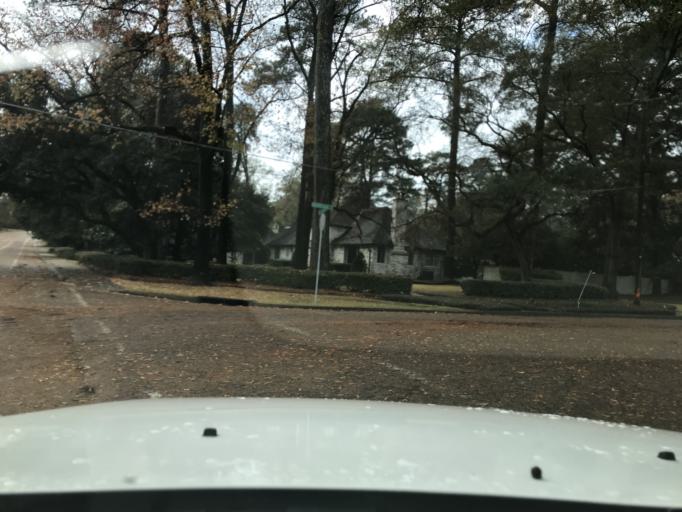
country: US
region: Mississippi
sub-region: Rankin County
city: Flowood
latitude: 32.3415
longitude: -90.1678
